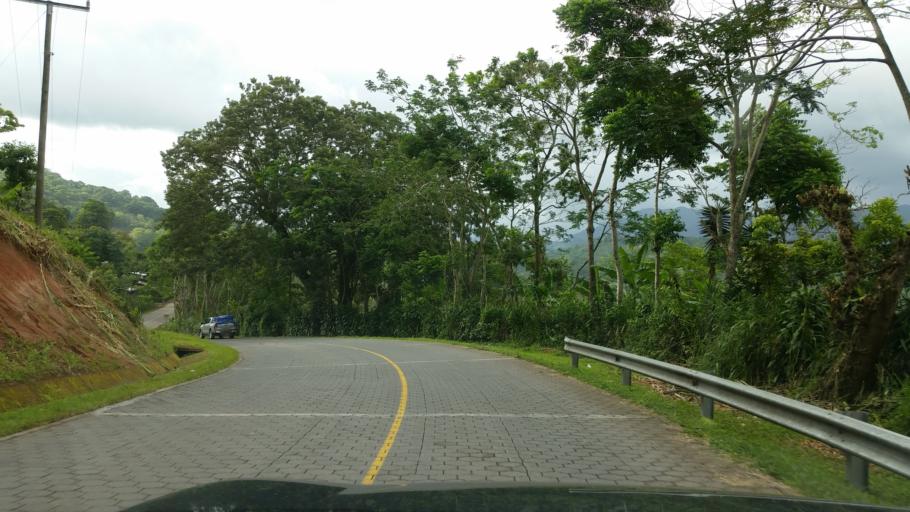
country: NI
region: Matagalpa
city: San Ramon
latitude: 13.1787
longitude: -85.7319
